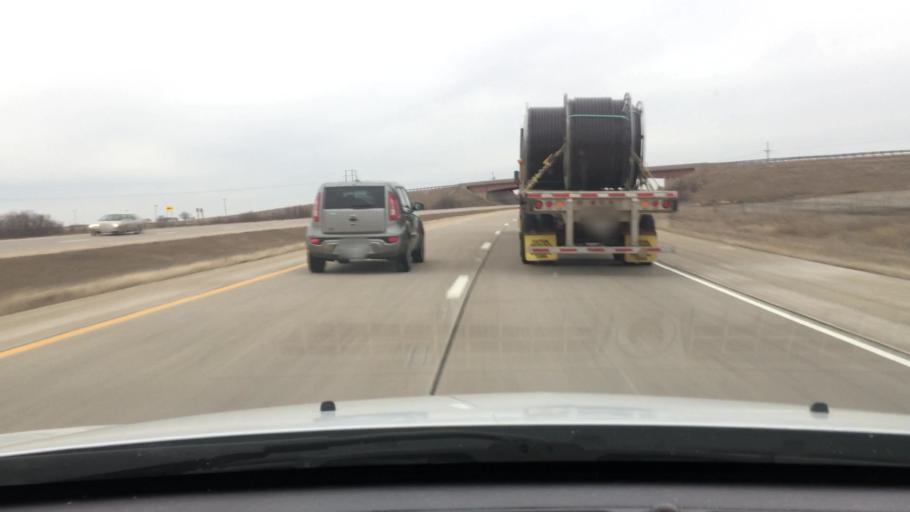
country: US
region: Illinois
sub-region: Woodford County
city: Minonk
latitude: 40.8951
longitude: -89.0533
